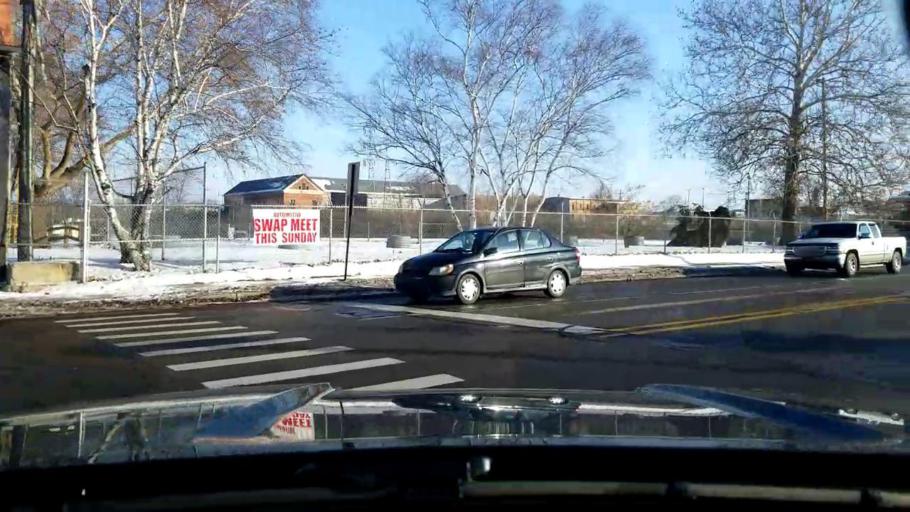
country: US
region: Michigan
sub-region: Jackson County
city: Jackson
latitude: 42.2546
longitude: -84.4088
